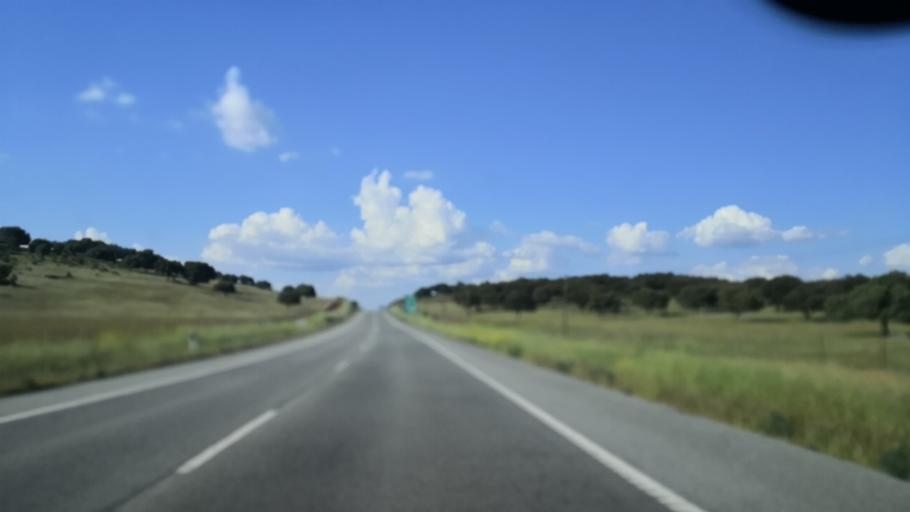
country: PT
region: Portalegre
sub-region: Arronches
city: Arronches
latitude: 39.0308
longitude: -7.4545
